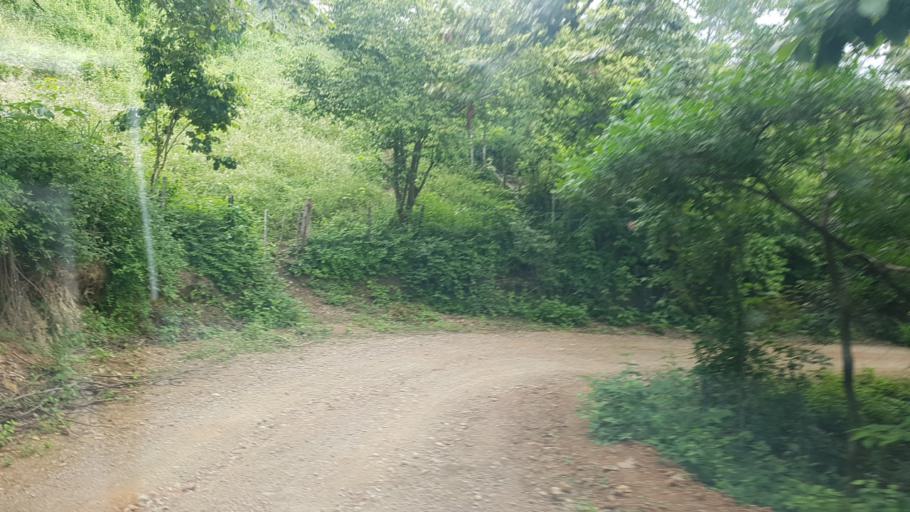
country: NI
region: Nueva Segovia
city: Ocotal
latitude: 13.5969
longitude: -86.4210
